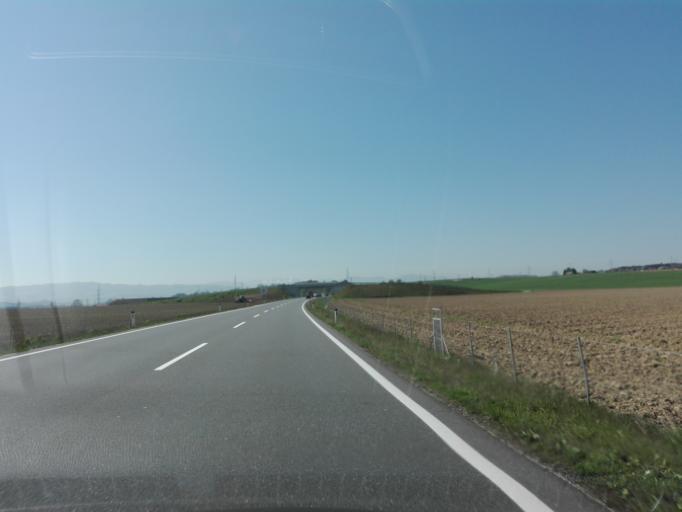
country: AT
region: Lower Austria
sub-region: Politischer Bezirk Amstetten
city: Haidershofen
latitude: 48.1128
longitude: 14.4483
